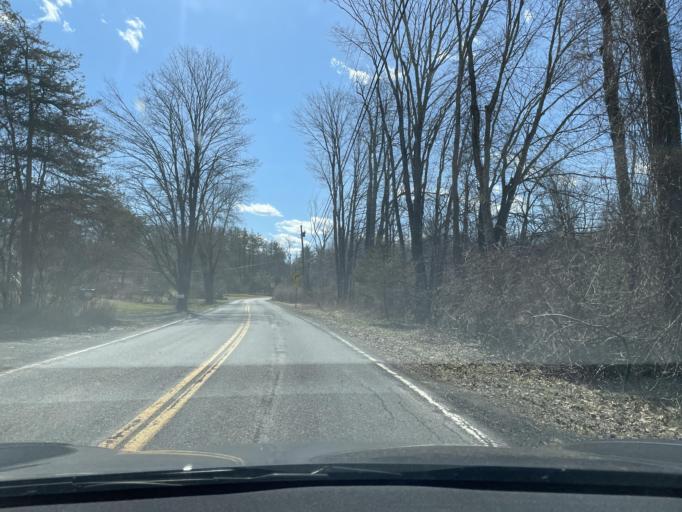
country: US
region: New York
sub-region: Ulster County
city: West Hurley
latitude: 41.9568
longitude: -74.1095
